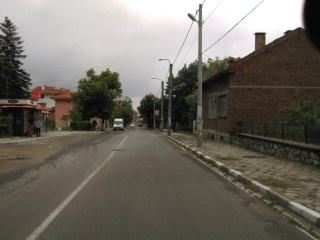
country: BG
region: Plovdiv
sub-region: Obshtina Karlovo
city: Karlovo
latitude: 42.6516
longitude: 24.7614
